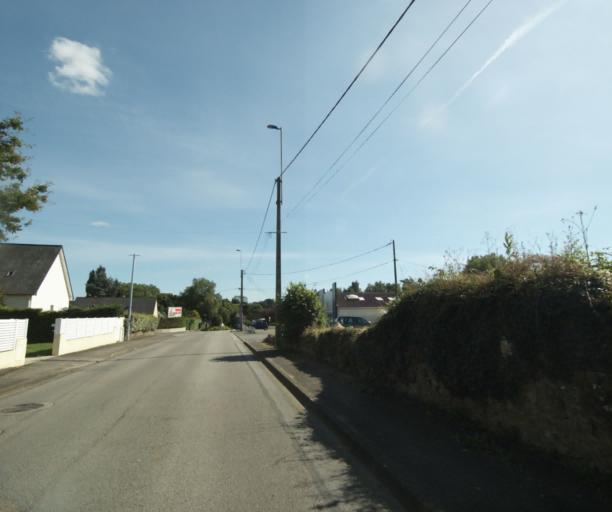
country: FR
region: Pays de la Loire
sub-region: Departement de la Mayenne
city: Laval
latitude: 48.0661
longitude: -0.7948
